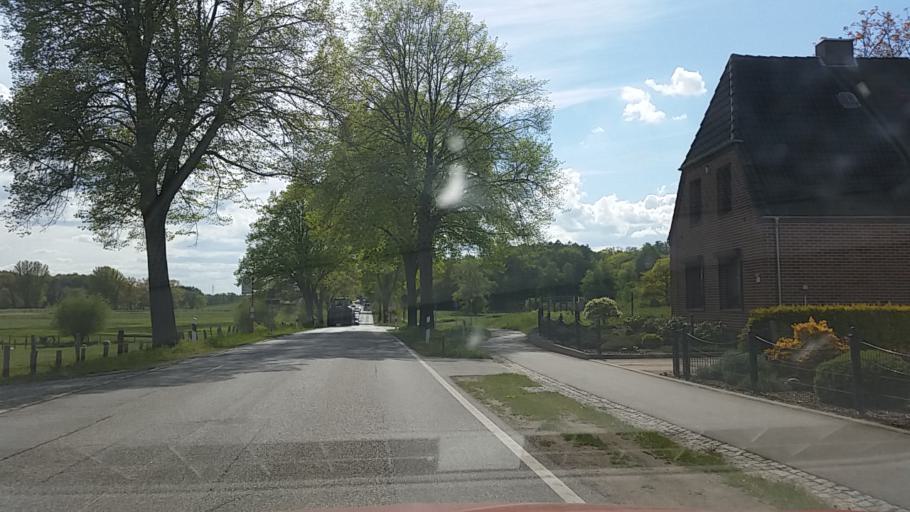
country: DE
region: Schleswig-Holstein
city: Meddewade
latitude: 53.8197
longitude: 10.4333
